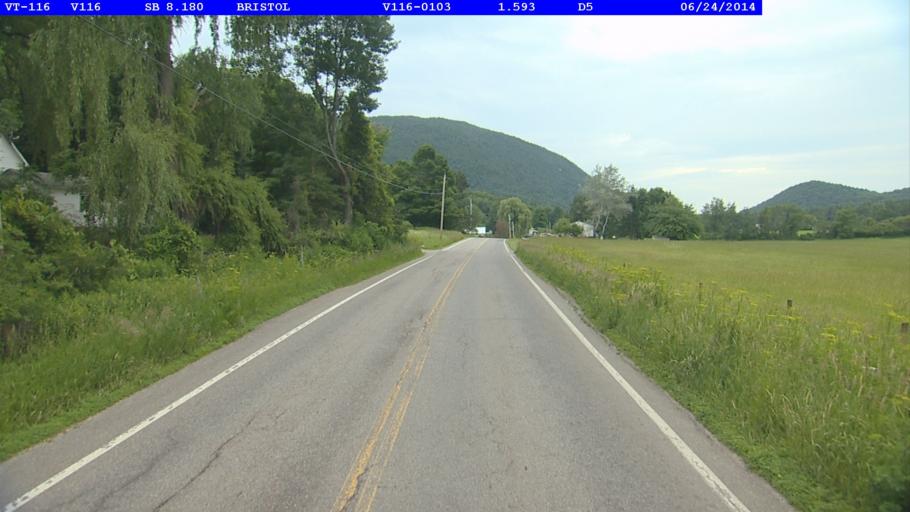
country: US
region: Vermont
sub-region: Addison County
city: Bristol
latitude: 44.0765
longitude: -73.0858
